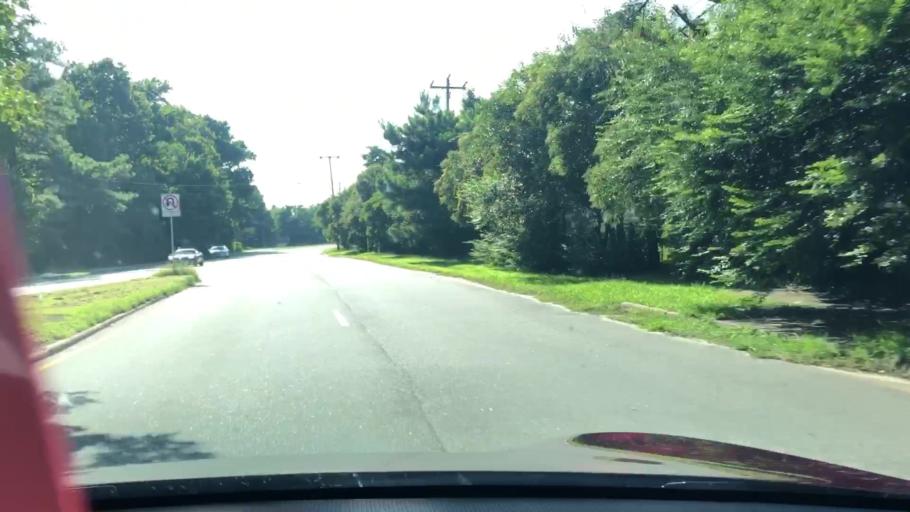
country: US
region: Virginia
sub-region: City of Virginia Beach
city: Virginia Beach
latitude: 36.8419
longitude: -75.9975
